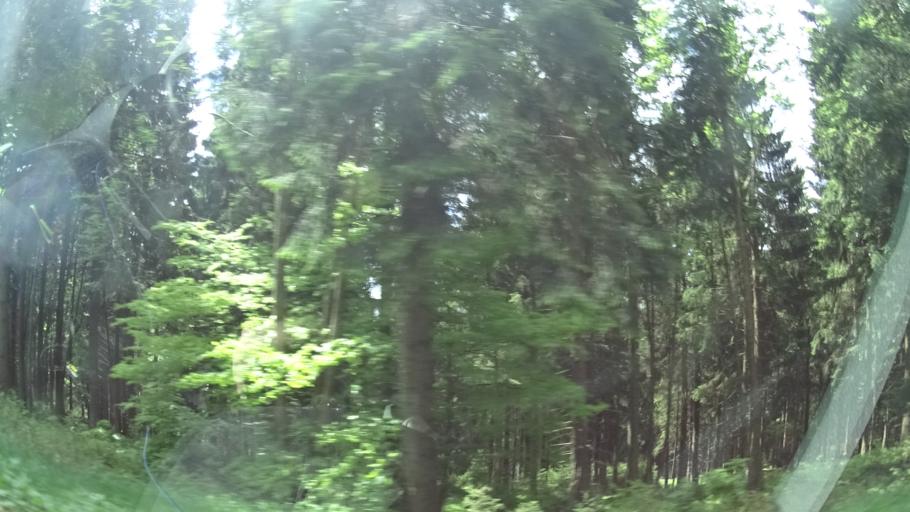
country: DE
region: Thuringia
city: Schmiedefeld am Rennsteig
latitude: 50.6201
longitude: 10.7745
